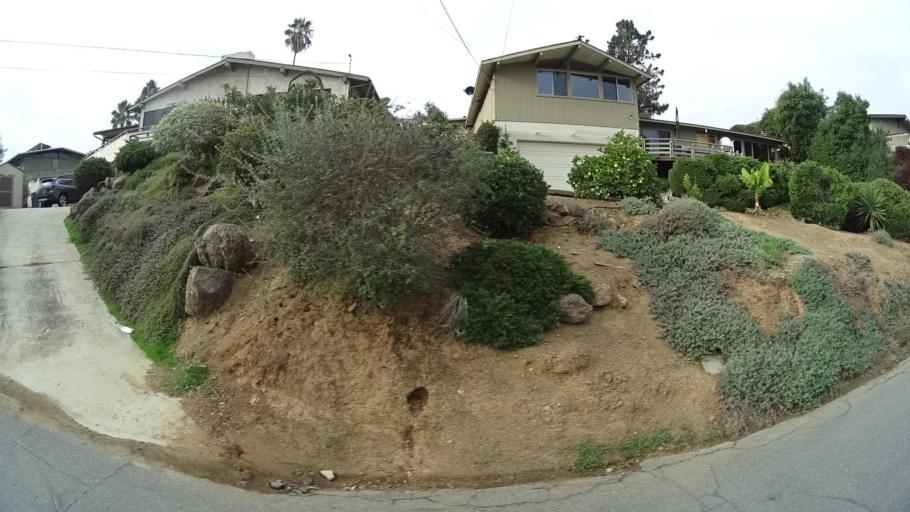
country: US
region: California
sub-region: San Diego County
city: Spring Valley
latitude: 32.7453
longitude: -117.0084
